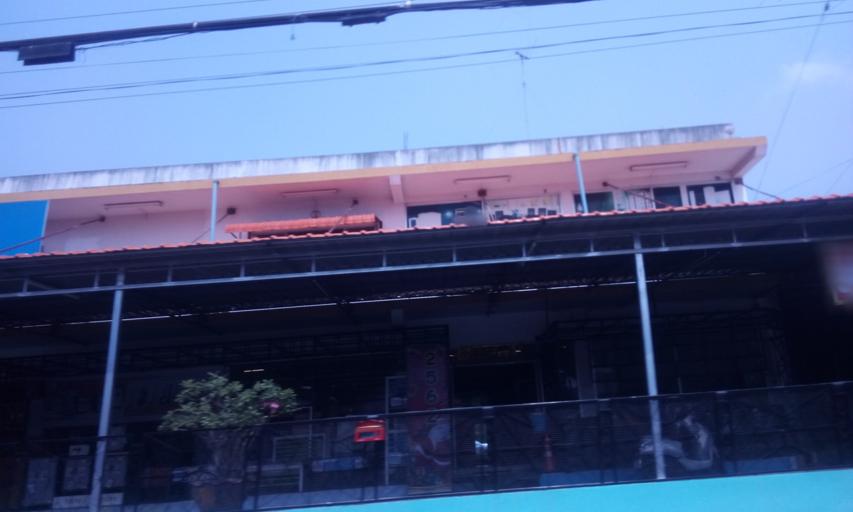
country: TH
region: Chon Buri
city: Phanat Nikhom
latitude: 13.4427
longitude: 101.1779
